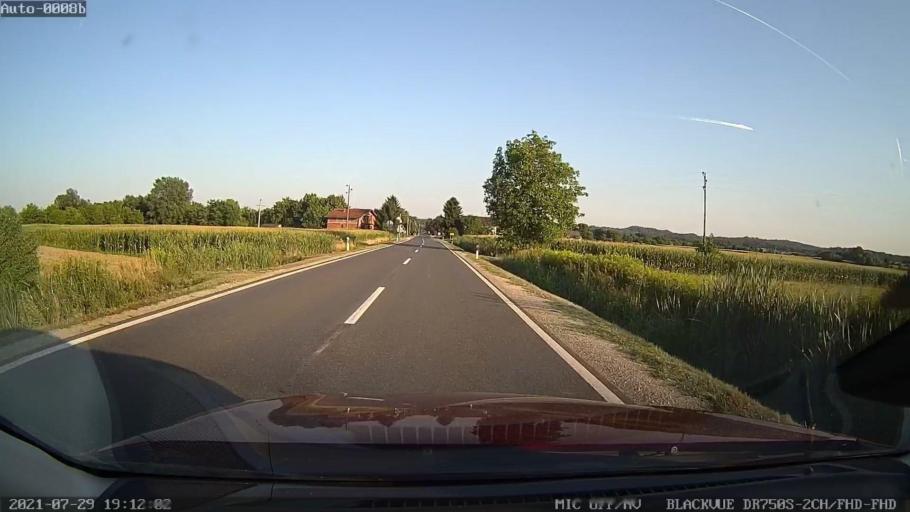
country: HR
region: Varazdinska
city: Jalzabet
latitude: 46.2710
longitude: 16.5138
